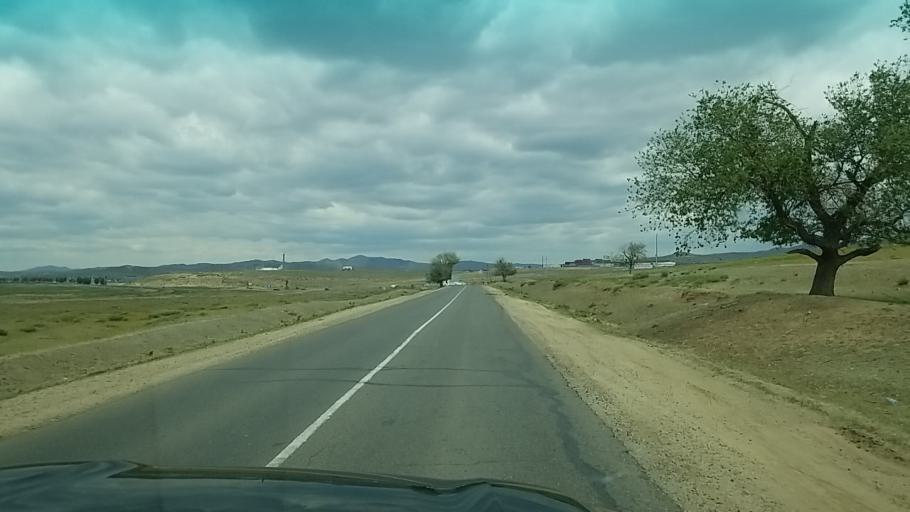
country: MN
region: Darhan Uul
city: Darhan
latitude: 49.4069
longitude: 105.9381
